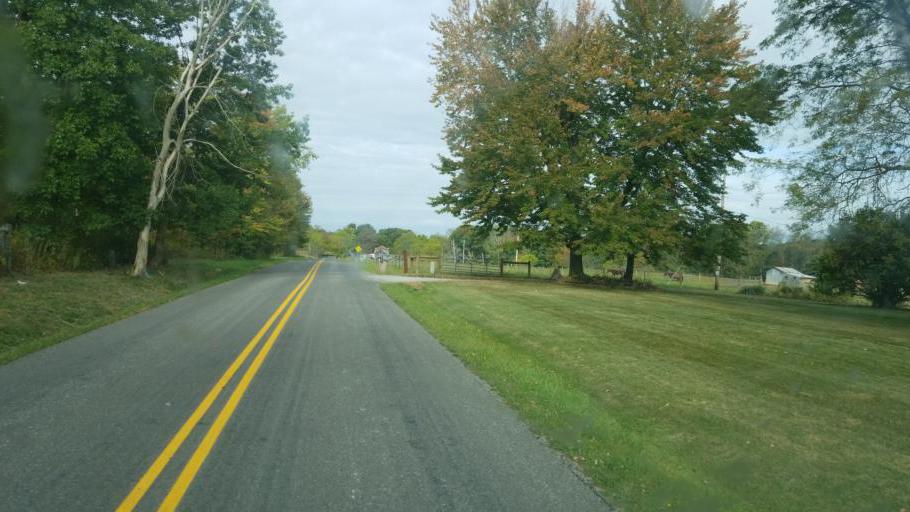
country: US
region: Pennsylvania
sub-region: Mercer County
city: Mercer
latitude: 41.3387
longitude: -80.2679
